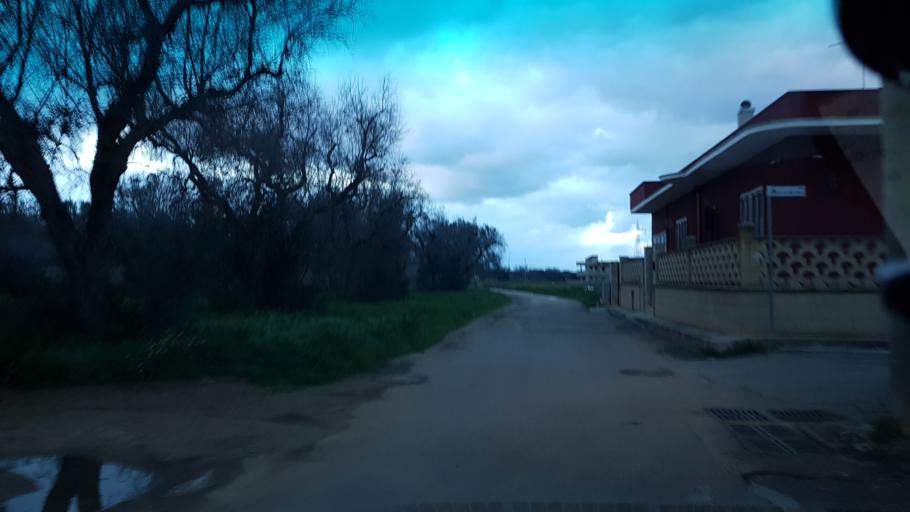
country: IT
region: Apulia
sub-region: Provincia di Brindisi
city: Torchiarolo
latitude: 40.4891
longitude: 18.0547
